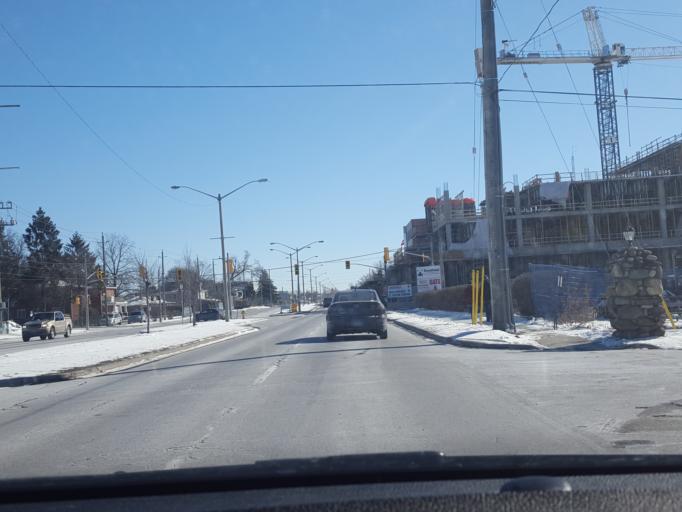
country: CA
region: Ontario
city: Cambridge
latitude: 43.3800
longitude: -80.3300
